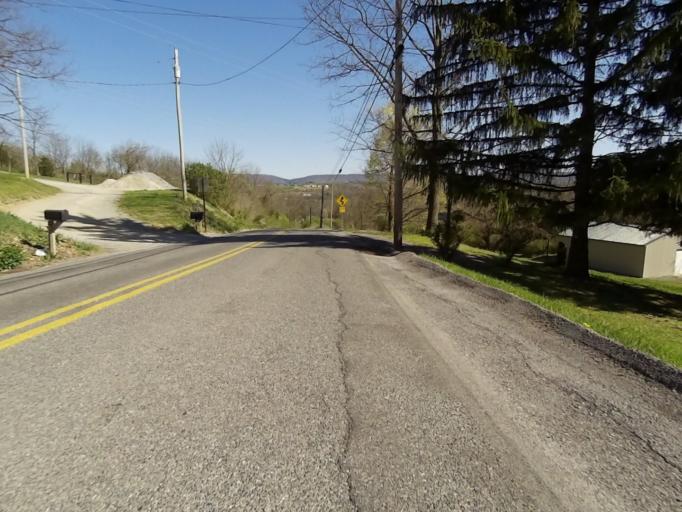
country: US
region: Pennsylvania
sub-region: Centre County
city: Bellefonte
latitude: 40.9117
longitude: -77.8028
